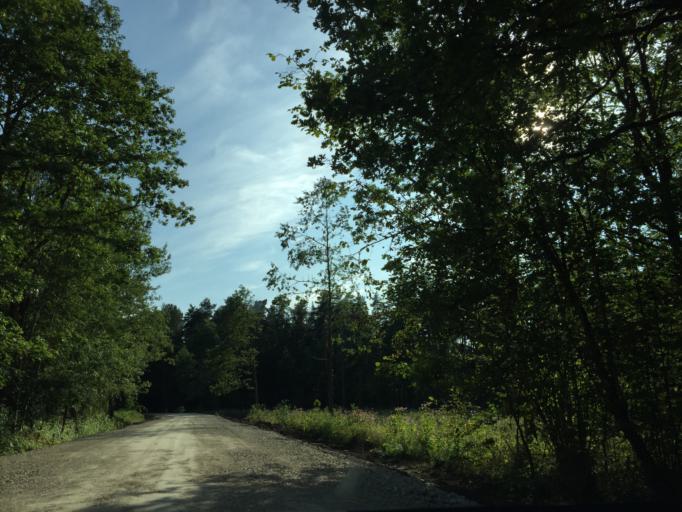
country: LV
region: Kegums
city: Kegums
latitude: 56.8108
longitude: 24.7465
